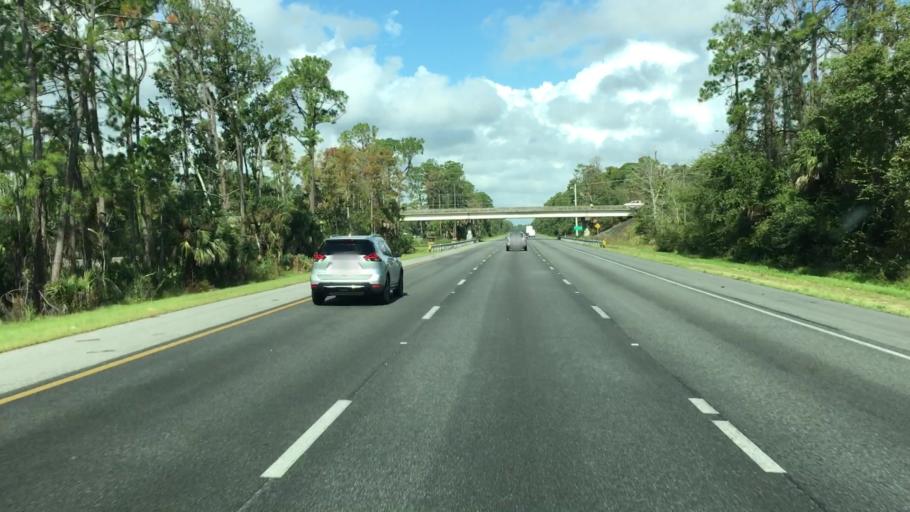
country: US
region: Florida
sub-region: Volusia County
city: Glencoe
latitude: 29.0459
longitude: -81.0066
